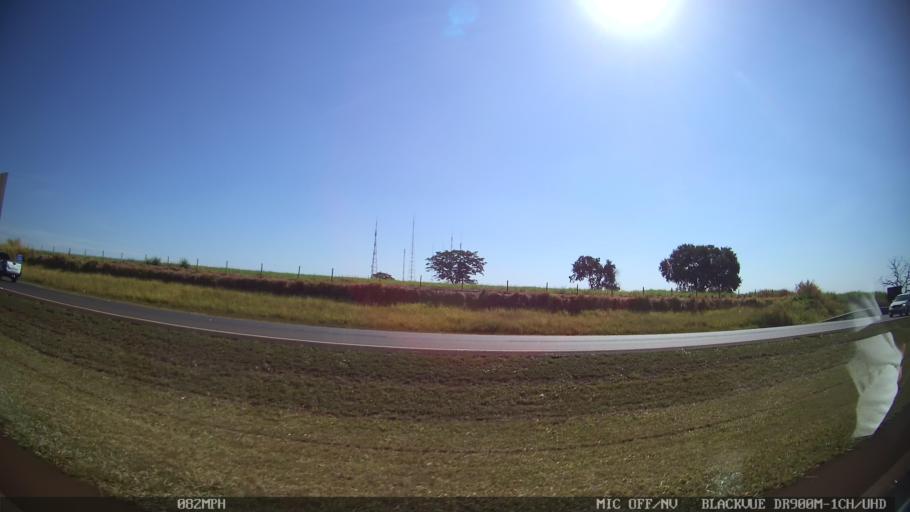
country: BR
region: Sao Paulo
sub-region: Ribeirao Preto
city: Ribeirao Preto
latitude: -21.1620
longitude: -47.8975
